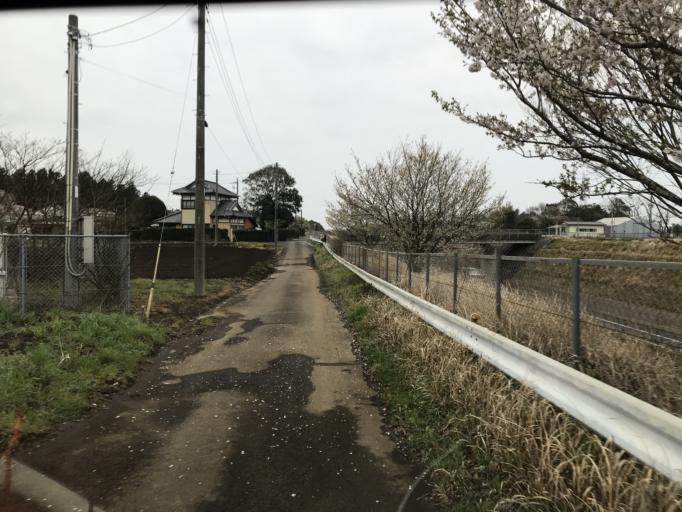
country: JP
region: Chiba
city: Sawara
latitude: 35.8516
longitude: 140.5134
